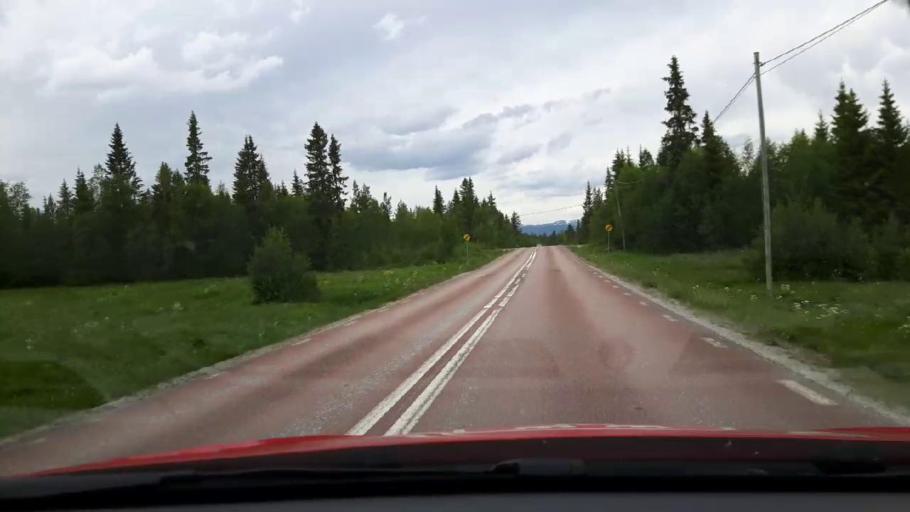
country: NO
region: Hedmark
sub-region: Engerdal
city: Engerdal
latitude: 62.5056
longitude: 12.6176
